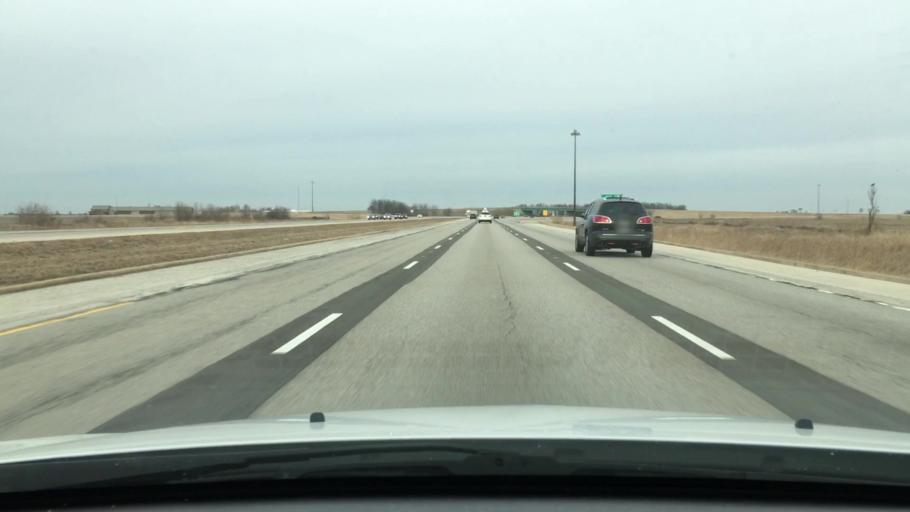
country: US
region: Illinois
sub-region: Sangamon County
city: Williamsville
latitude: 40.0137
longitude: -89.4990
